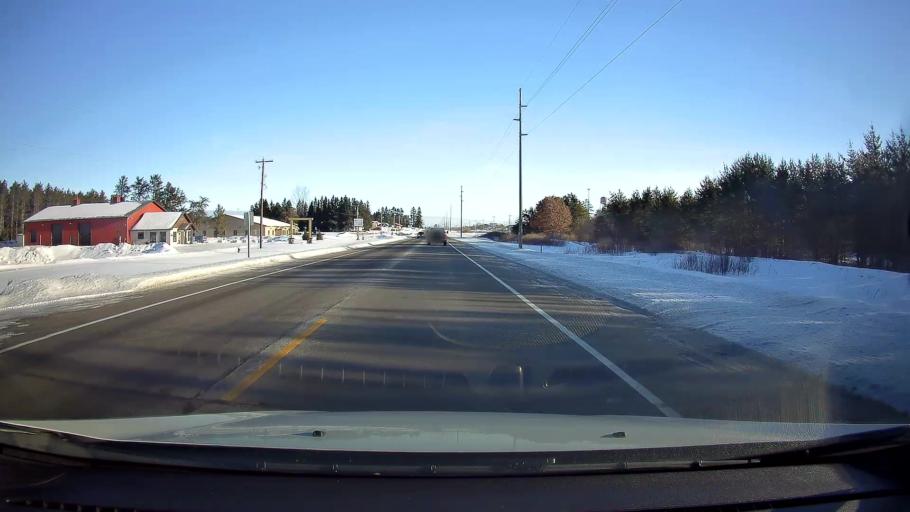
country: US
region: Wisconsin
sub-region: Sawyer County
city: Hayward
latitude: 46.0028
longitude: -91.4997
